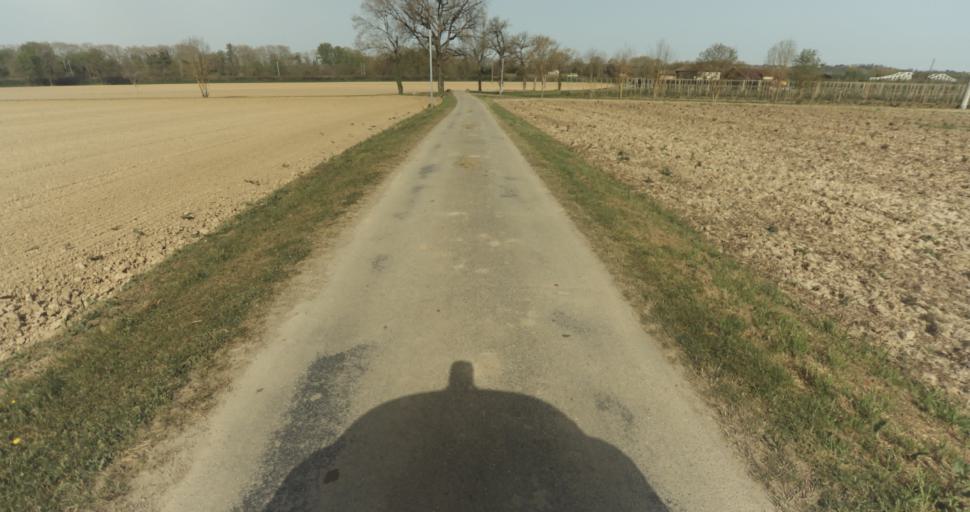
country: FR
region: Midi-Pyrenees
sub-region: Departement du Tarn-et-Garonne
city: Moissac
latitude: 44.0819
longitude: 1.1077
